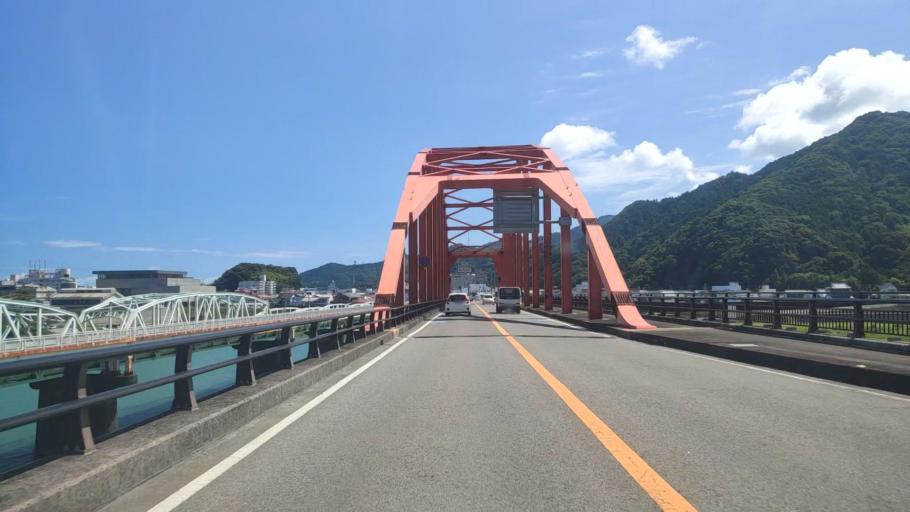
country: JP
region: Wakayama
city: Shingu
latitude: 33.7345
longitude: 135.9880
